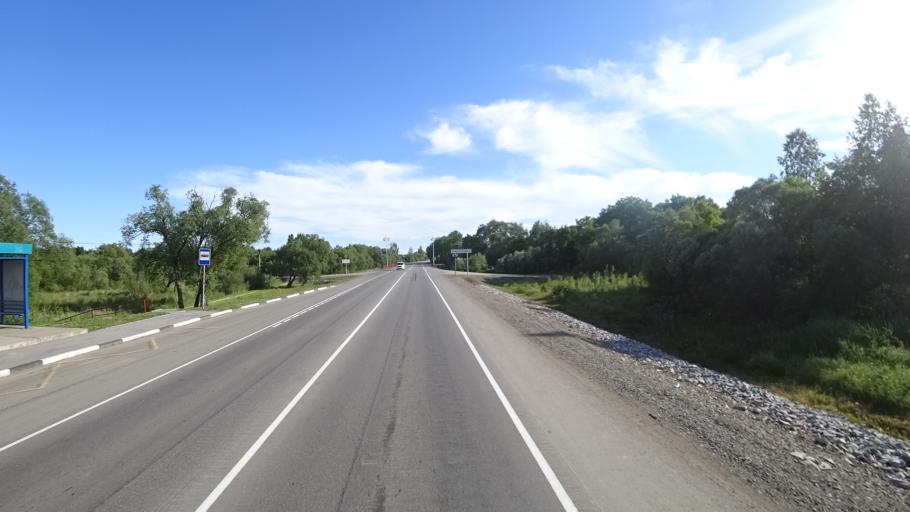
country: RU
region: Khabarovsk Krai
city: Khor
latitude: 47.8573
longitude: 134.9623
